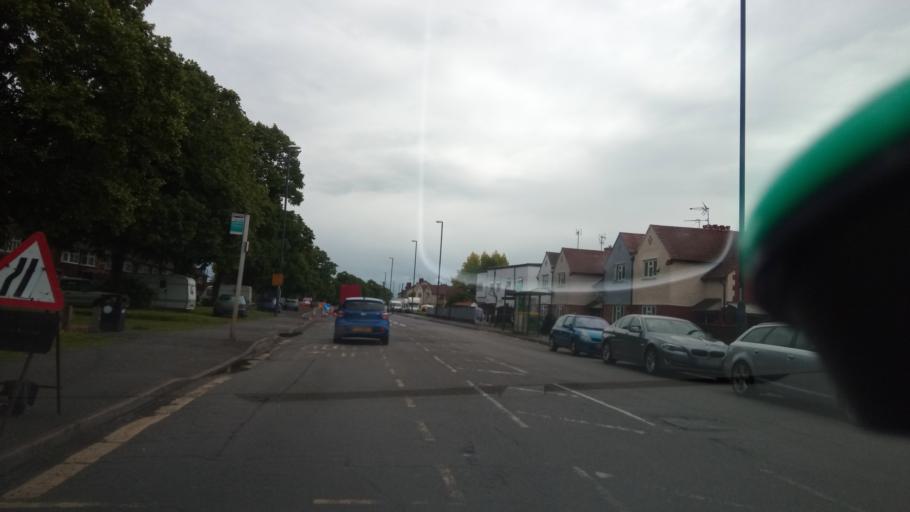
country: GB
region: England
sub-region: Derby
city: Derby
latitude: 52.8955
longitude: -1.4560
